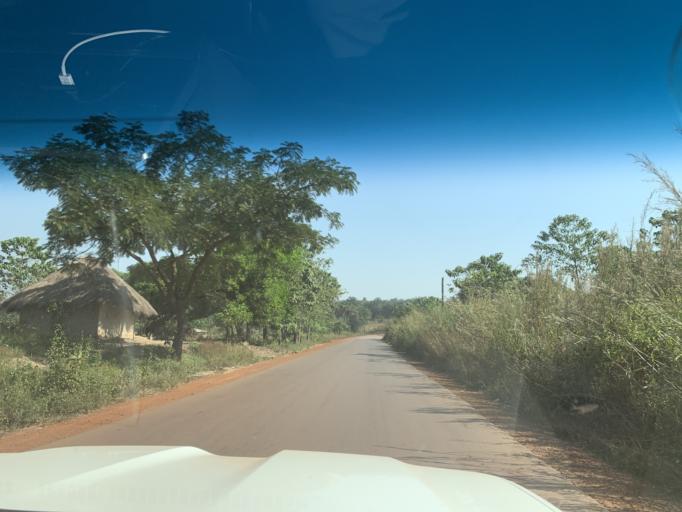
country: GN
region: Kindia
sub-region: Kindia
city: Kindia
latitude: 9.8945
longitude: -13.0499
